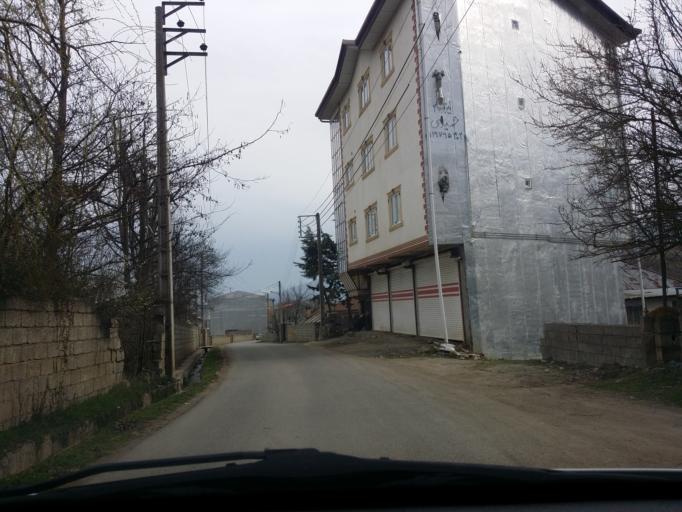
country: IR
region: Mazandaran
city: `Abbasabad
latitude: 36.5474
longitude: 51.1671
